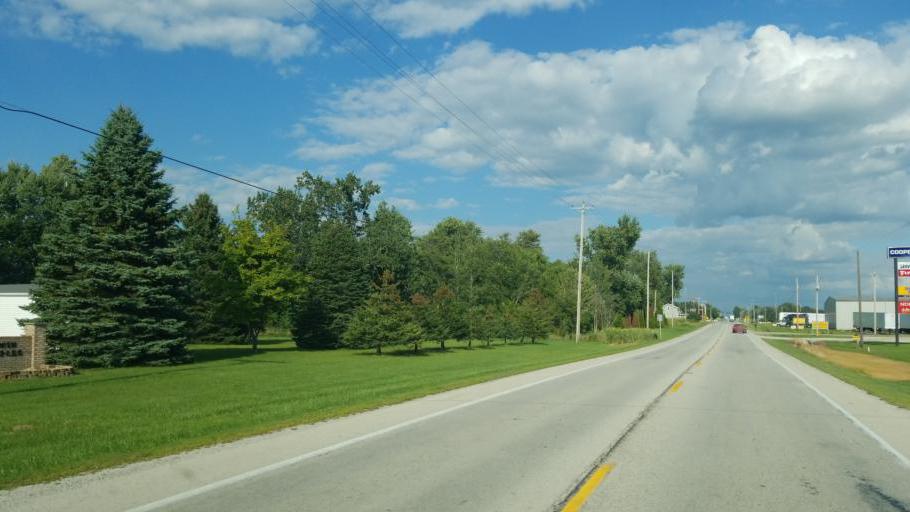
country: US
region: Ohio
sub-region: Wood County
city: Pemberville
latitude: 41.3412
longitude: -83.4237
